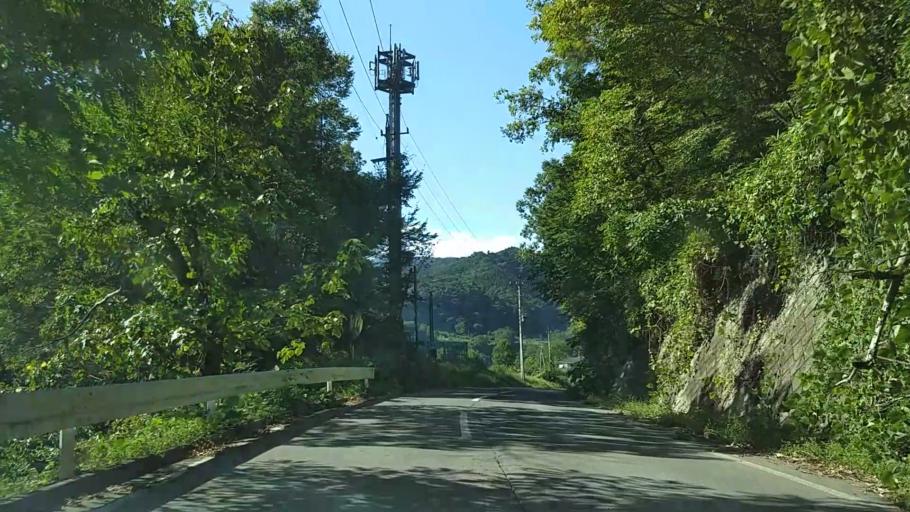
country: JP
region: Nagano
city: Nagano-shi
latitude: 36.6082
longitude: 138.0896
